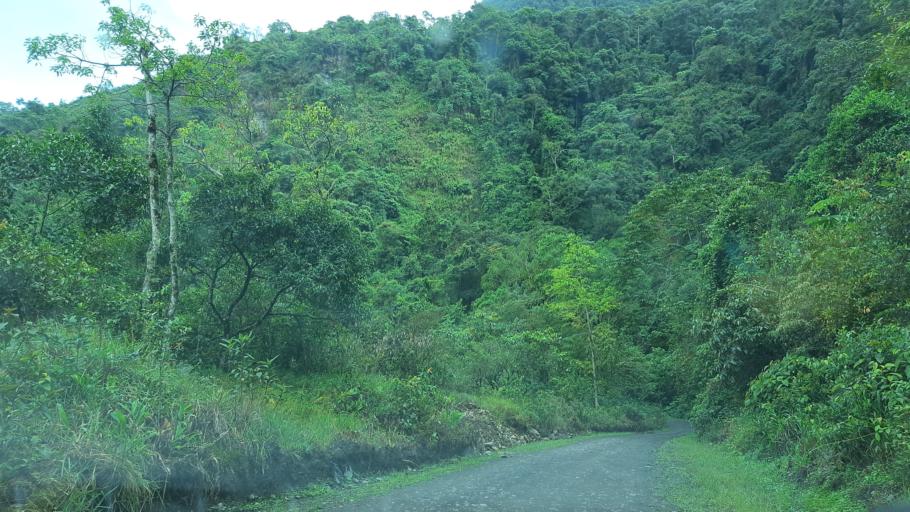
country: CO
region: Boyaca
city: Chivor
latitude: 4.9130
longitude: -73.3099
